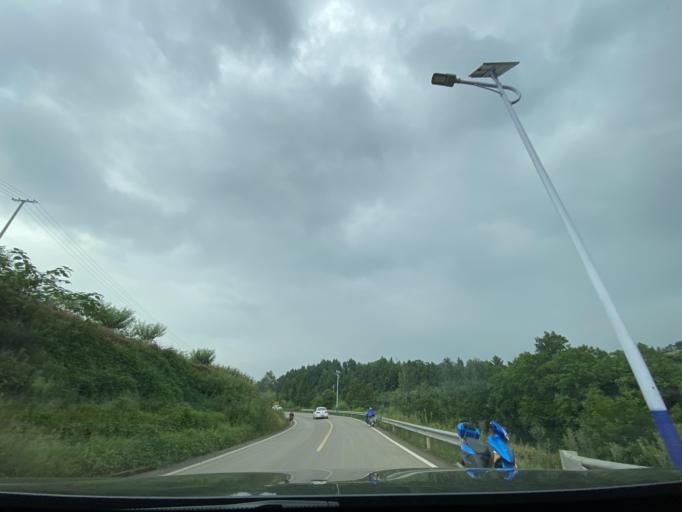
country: CN
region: Sichuan
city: Jiancheng
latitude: 30.5512
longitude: 104.5237
